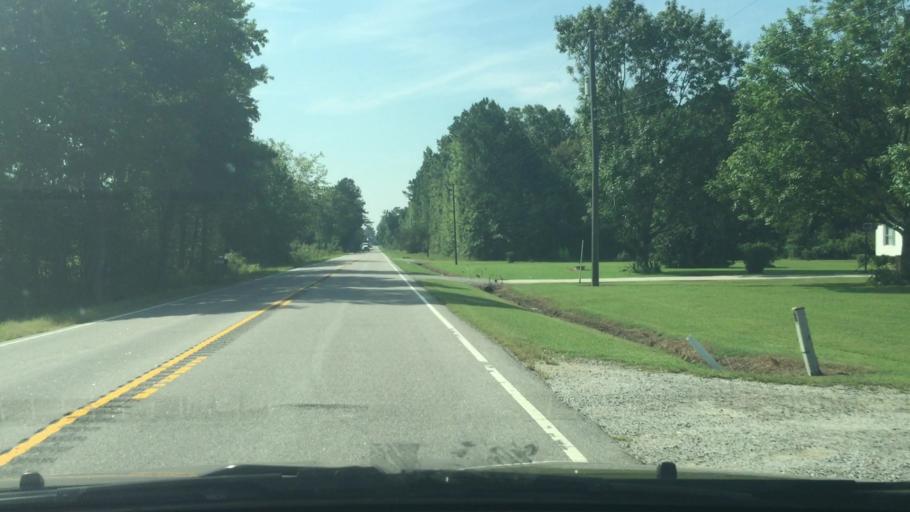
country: US
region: Virginia
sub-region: Southampton County
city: Courtland
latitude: 36.8360
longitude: -77.1287
